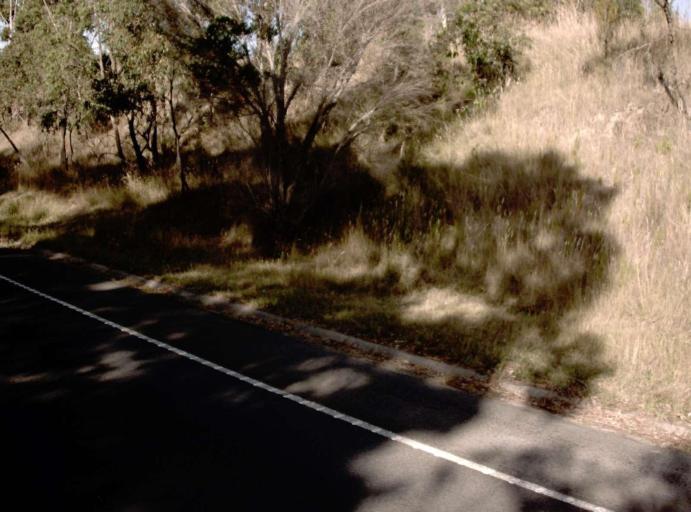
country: AU
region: Victoria
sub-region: Latrobe
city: Morwell
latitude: -38.3299
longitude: 146.4159
